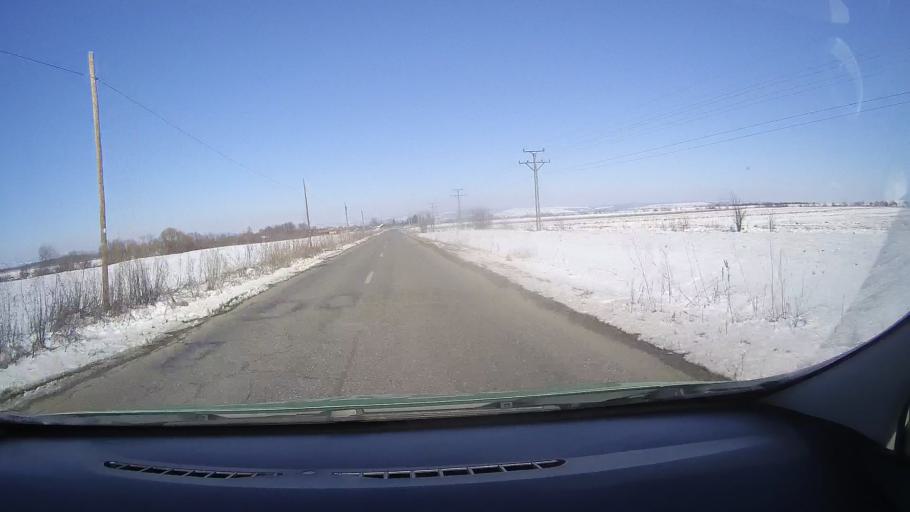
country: RO
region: Brasov
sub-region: Comuna Harseni
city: Harseni
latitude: 45.7759
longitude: 25.0011
